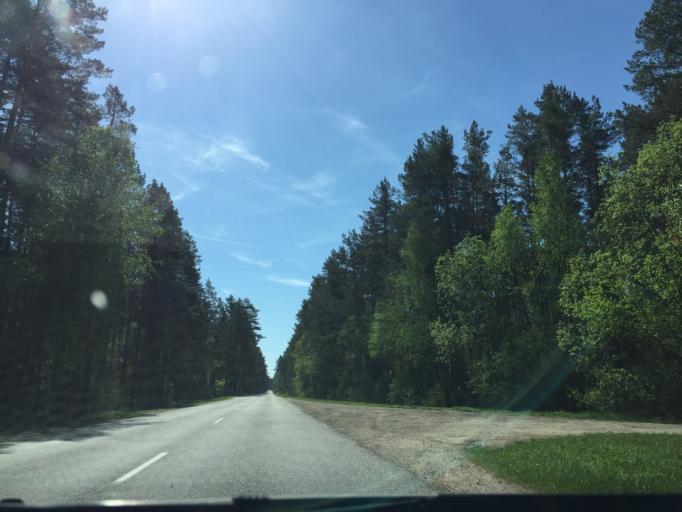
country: LV
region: Garkalne
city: Garkalne
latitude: 57.0346
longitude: 24.4202
